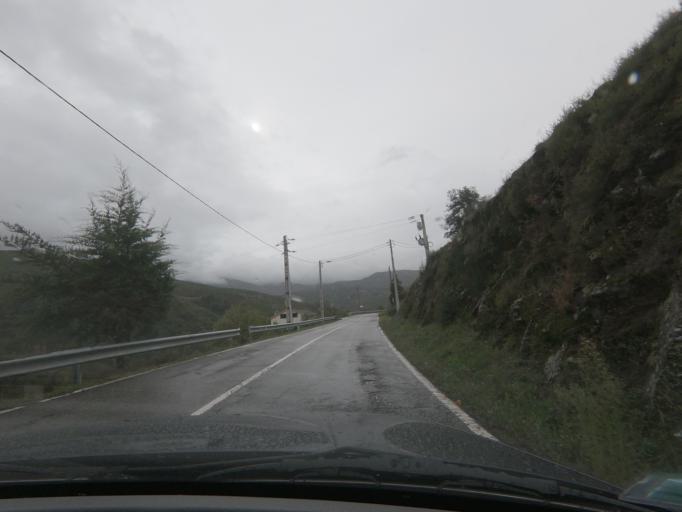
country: PT
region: Vila Real
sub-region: Mondim de Basto
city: Mondim de Basto
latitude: 41.3490
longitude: -7.8879
